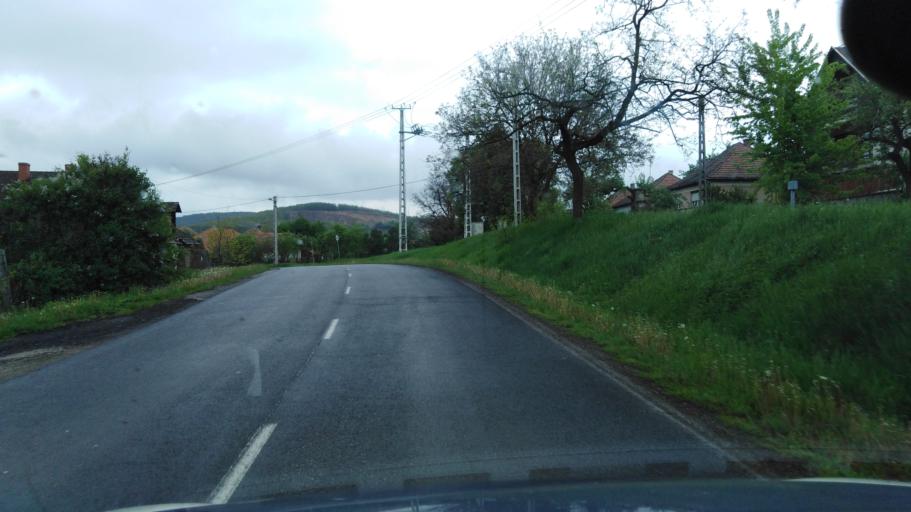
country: HU
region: Nograd
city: Rimoc
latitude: 47.9965
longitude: 19.6197
